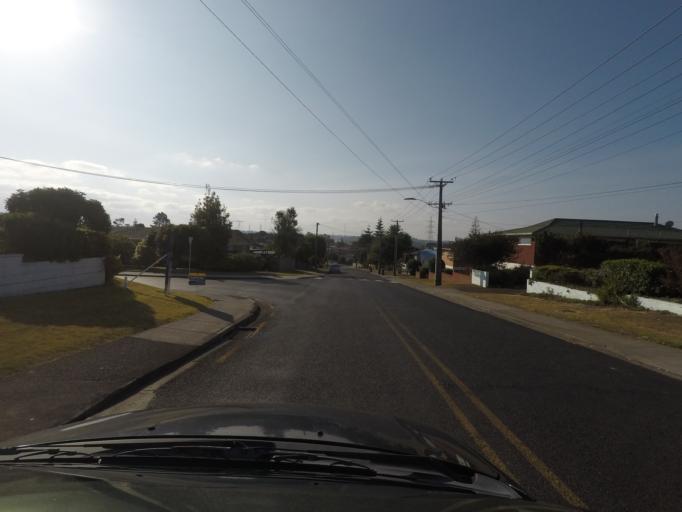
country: NZ
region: Auckland
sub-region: Auckland
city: Rosebank
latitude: -36.8586
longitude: 174.6501
